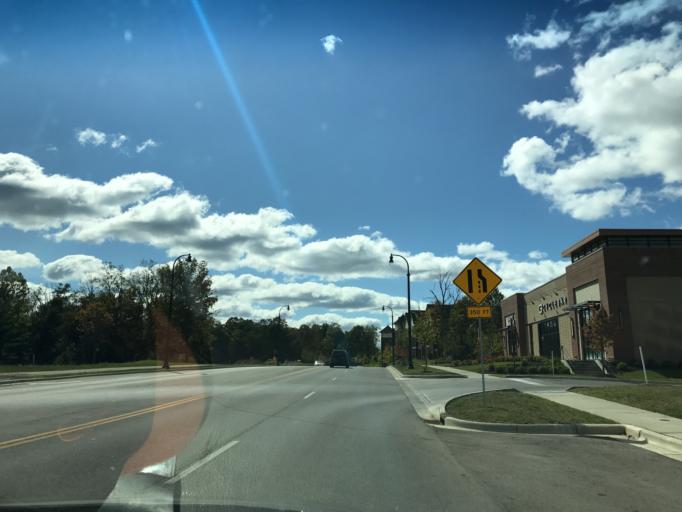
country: US
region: Ohio
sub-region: Franklin County
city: Westerville
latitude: 40.1447
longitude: -82.9563
